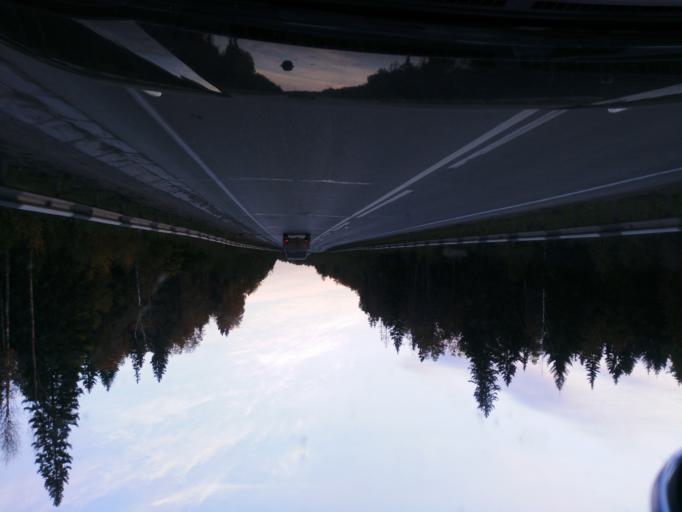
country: RU
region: Perm
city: Novyye Lyady
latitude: 58.0924
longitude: 56.4274
